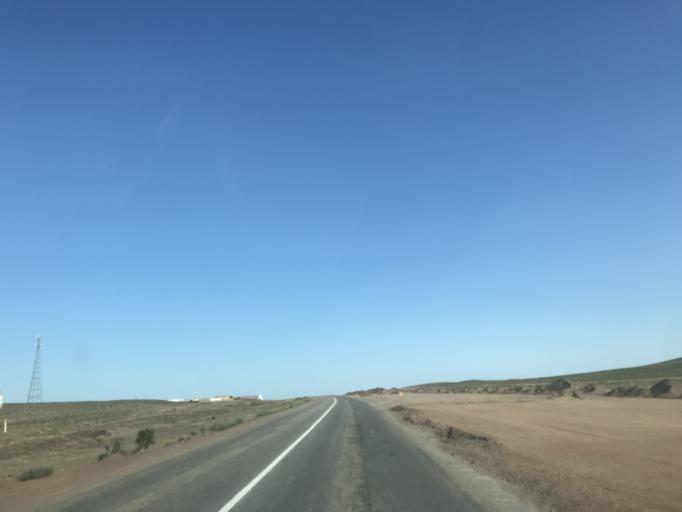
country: KZ
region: Zhambyl
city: Mynaral
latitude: 45.3296
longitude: 73.7282
